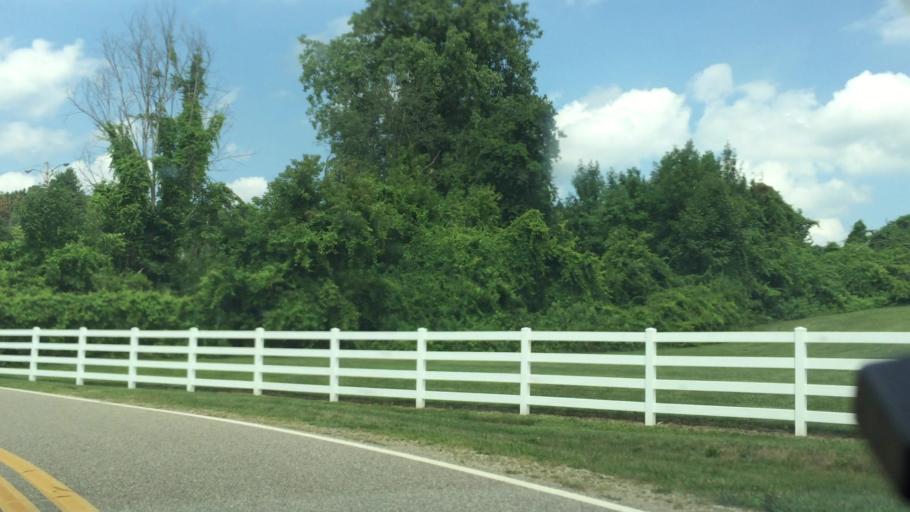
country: US
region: Michigan
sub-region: Oakland County
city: Auburn Hills
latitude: 42.6753
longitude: -83.2002
